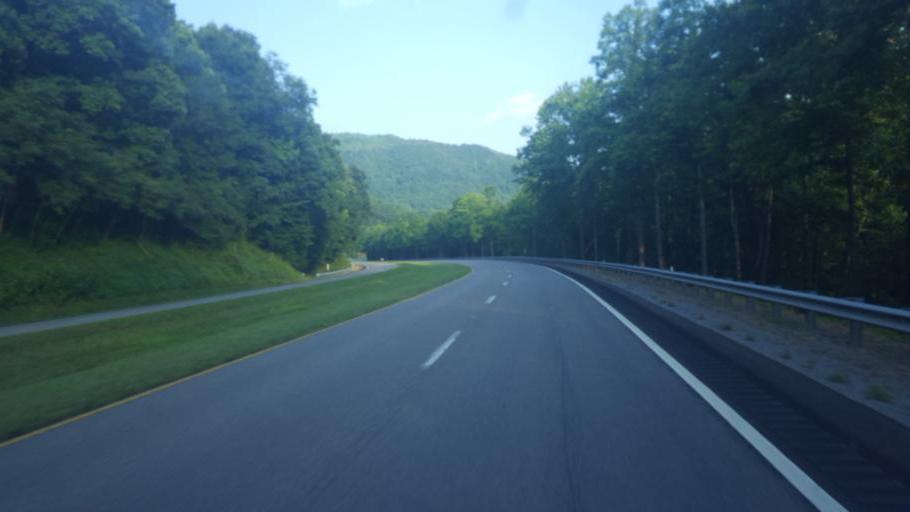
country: US
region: Virginia
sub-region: Lee County
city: Dryden
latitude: 36.7548
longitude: -82.8090
